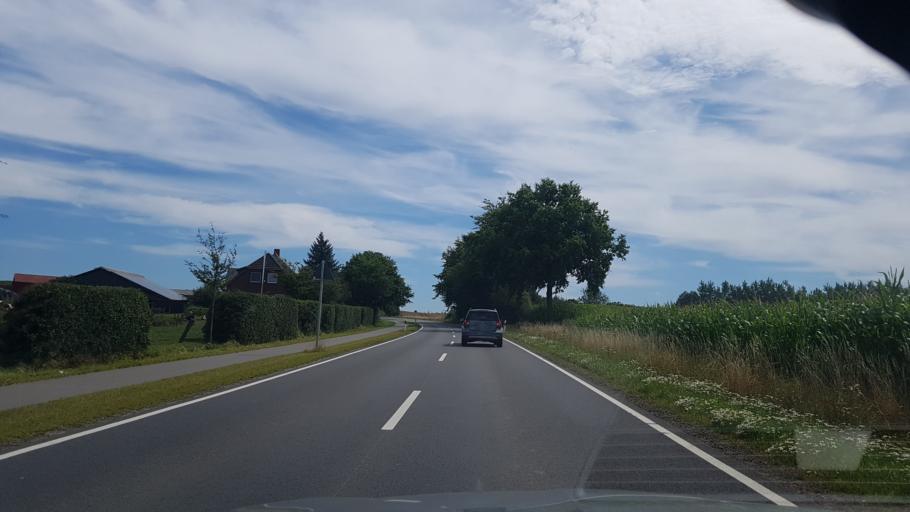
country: DE
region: Schleswig-Holstein
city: Warnau
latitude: 54.1691
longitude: 10.1569
